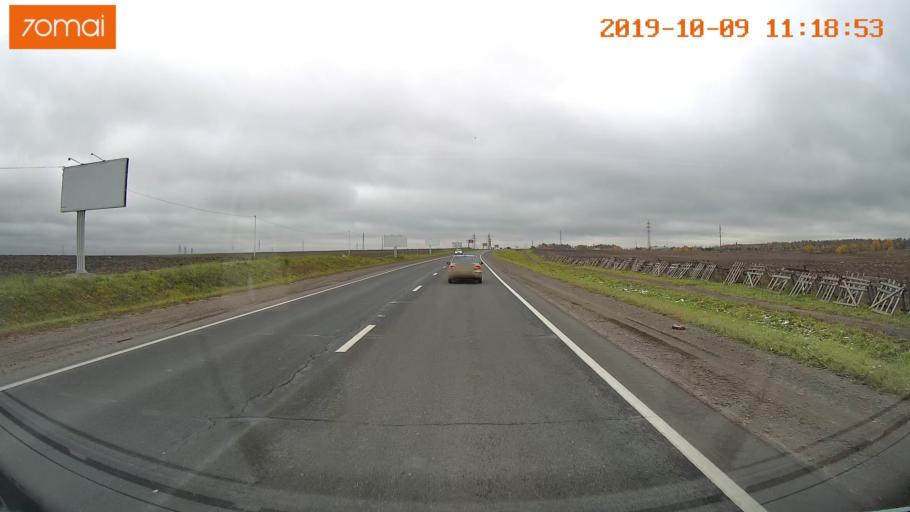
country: RU
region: Vologda
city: Vologda
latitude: 59.1640
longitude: 39.9213
